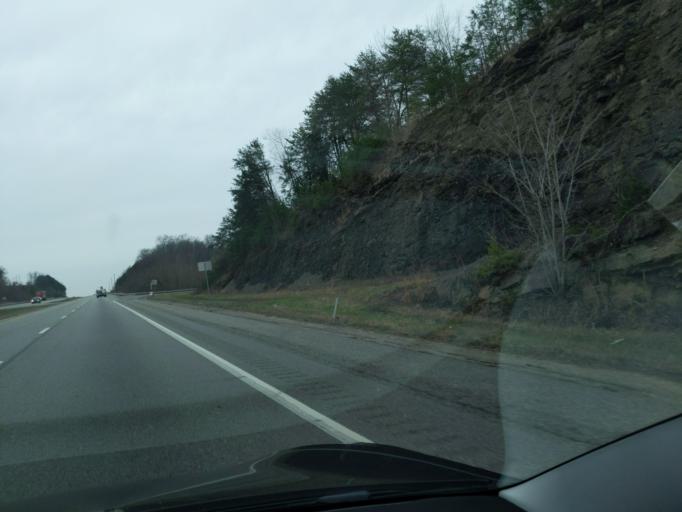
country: US
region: Kentucky
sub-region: Knox County
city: Barbourville
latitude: 36.8357
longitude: -83.7807
